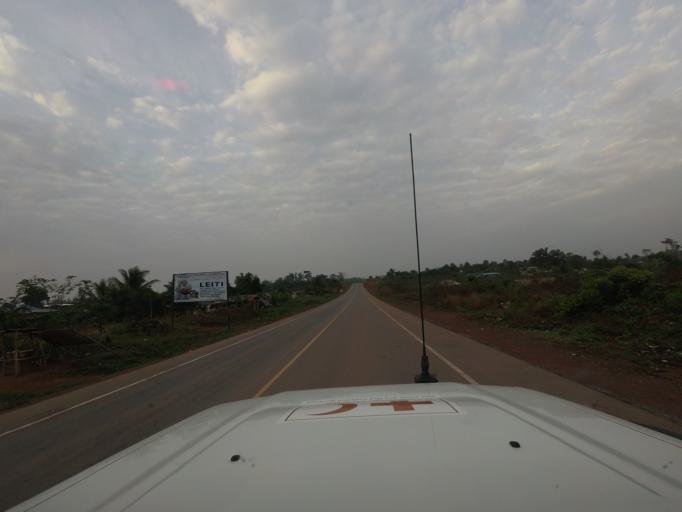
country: LR
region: Nimba
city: Sanniquellie
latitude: 7.2140
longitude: -9.0110
